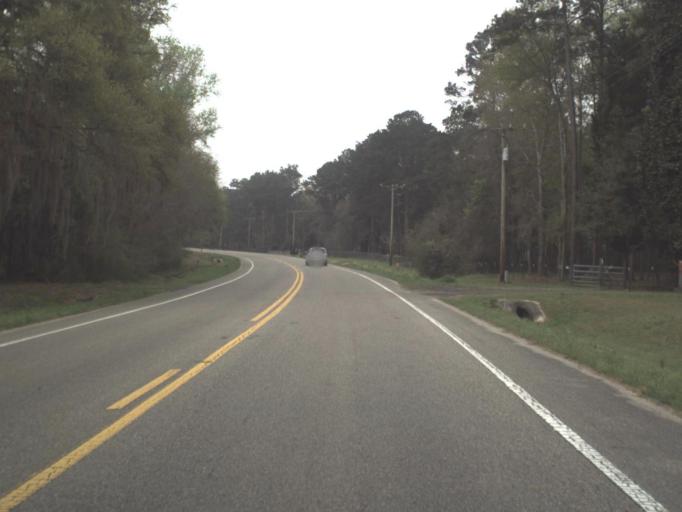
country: US
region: Florida
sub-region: Gadsden County
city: Gretna
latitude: 30.5628
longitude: -84.6768
